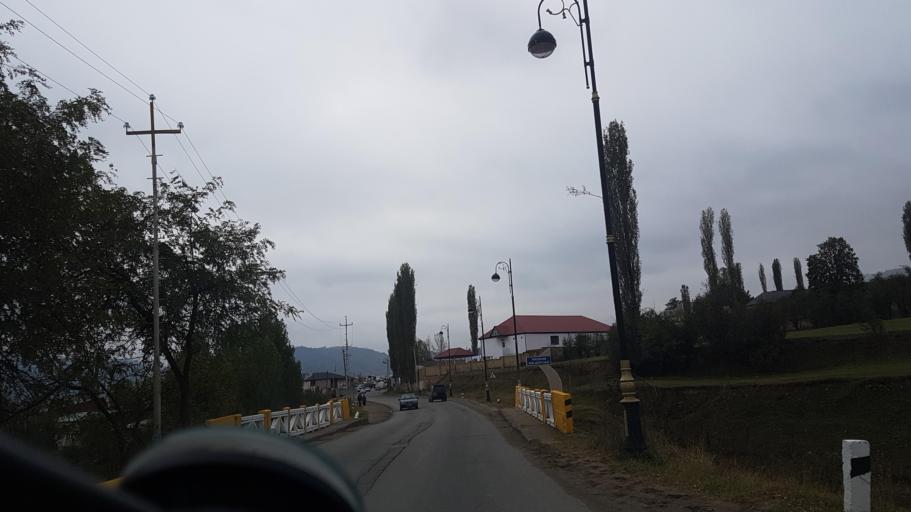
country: AZ
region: Gadabay Rayon
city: Ariqdam
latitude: 40.5948
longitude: 45.8108
